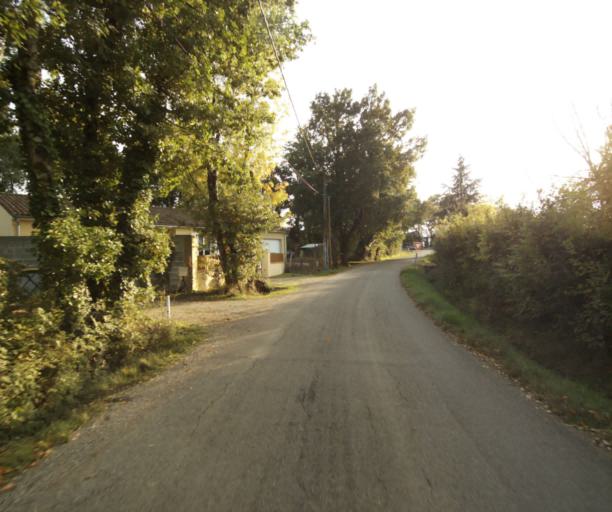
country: FR
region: Midi-Pyrenees
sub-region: Departement du Tarn-et-Garonne
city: Labastide-Saint-Pierre
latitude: 43.9160
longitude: 1.3505
